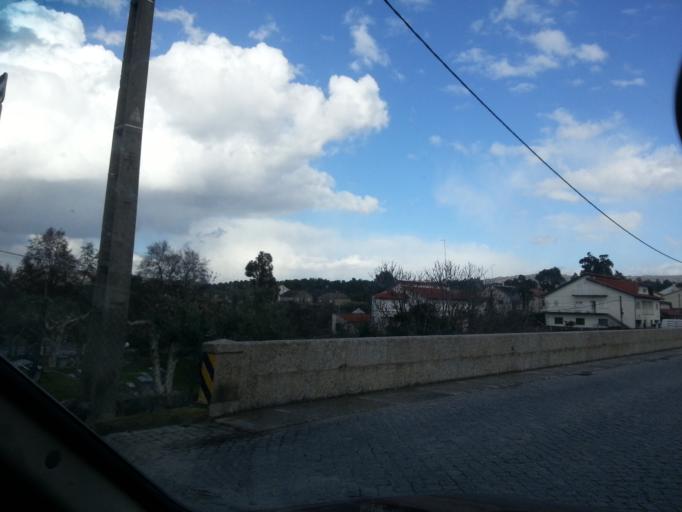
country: PT
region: Guarda
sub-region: Celorico da Beira
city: Celorico da Beira
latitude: 40.6264
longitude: -7.3362
